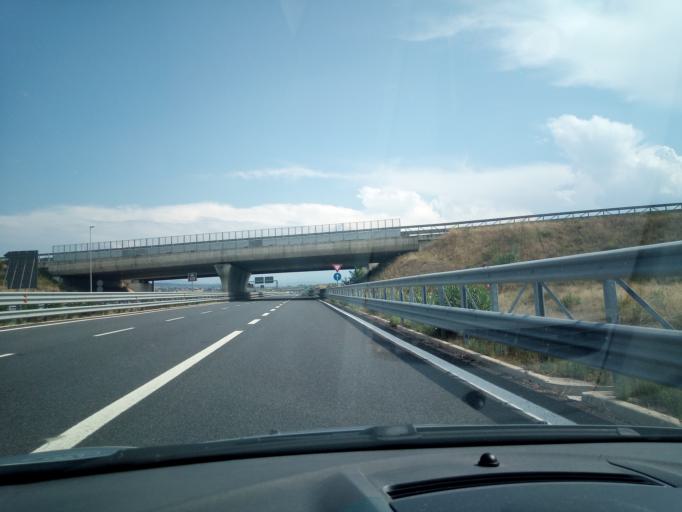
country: IT
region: Calabria
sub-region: Provincia di Cosenza
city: Firmo
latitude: 39.7220
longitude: 16.2387
